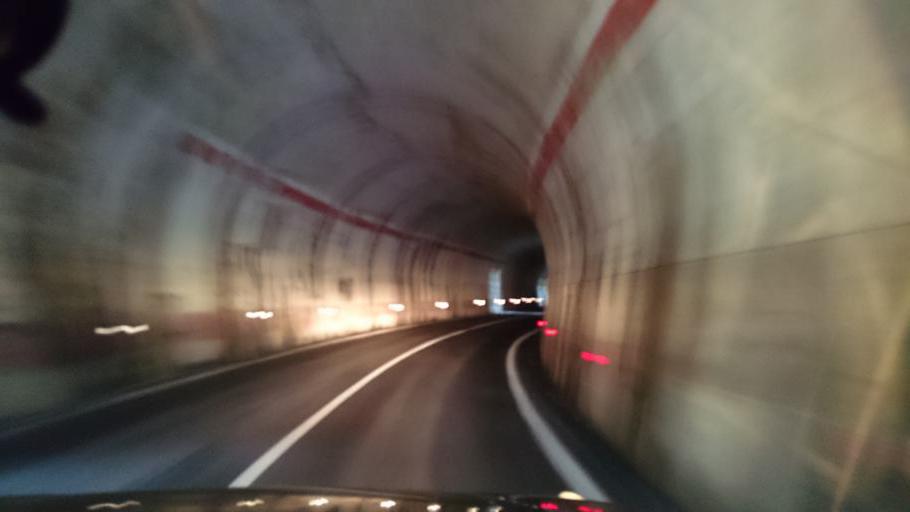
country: IT
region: Friuli Venezia Giulia
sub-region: Provincia di Udine
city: Tarvisio
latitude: 46.4233
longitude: 13.5704
